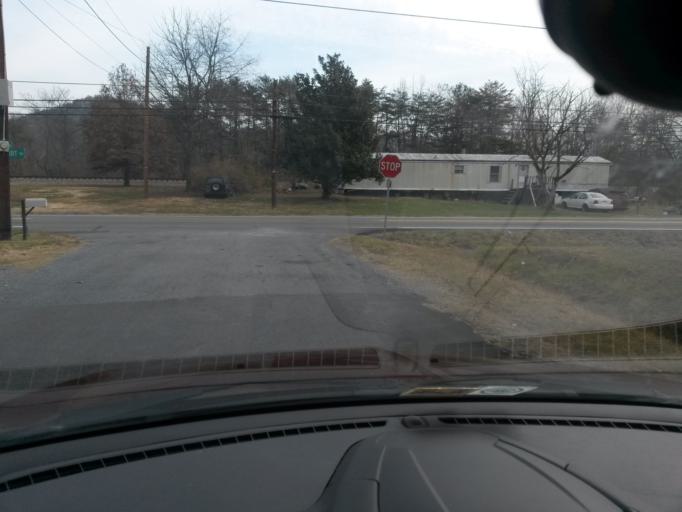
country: US
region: Virginia
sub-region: Alleghany County
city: Clifton Forge
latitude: 37.7909
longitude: -79.7852
